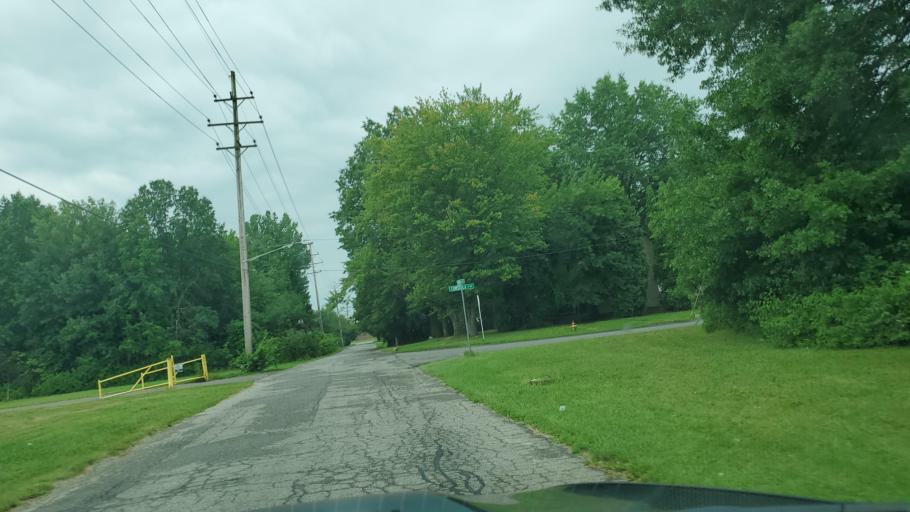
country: US
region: Ohio
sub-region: Trumbull County
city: Warren
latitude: 41.2543
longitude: -80.8134
